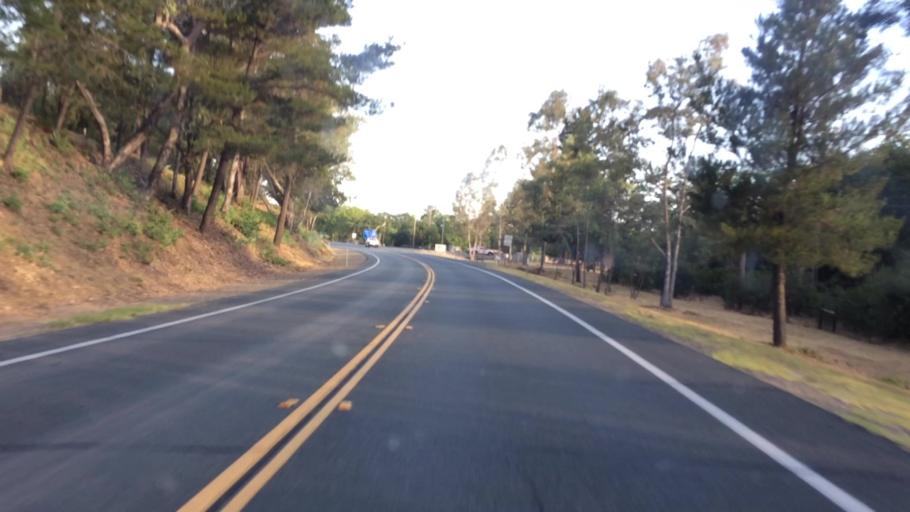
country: US
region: California
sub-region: Amador County
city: Ione
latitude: 38.3625
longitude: -120.9426
